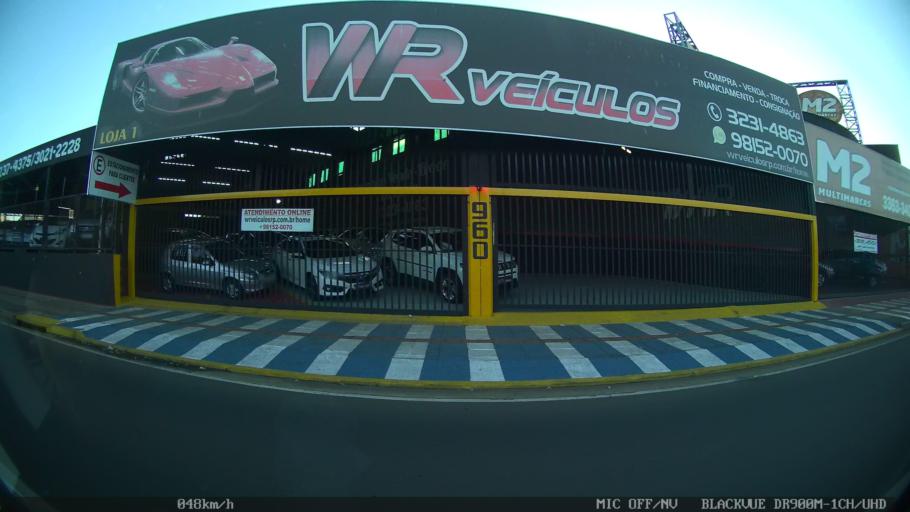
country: BR
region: Sao Paulo
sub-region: Sao Jose Do Rio Preto
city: Sao Jose do Rio Preto
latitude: -20.7881
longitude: -49.3771
